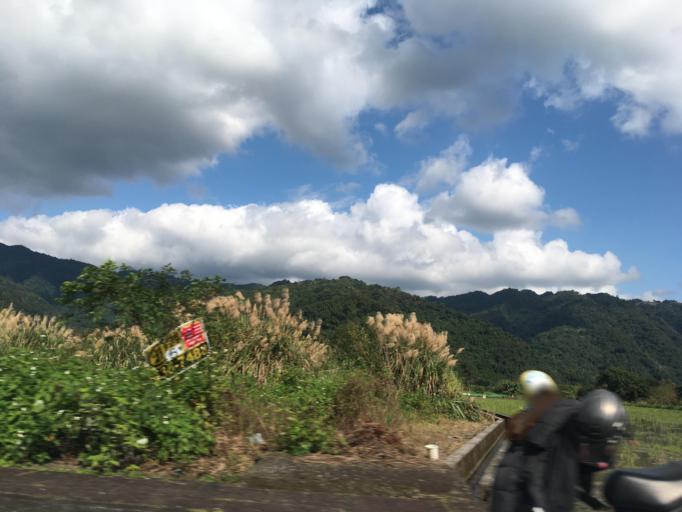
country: TW
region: Taiwan
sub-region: Yilan
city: Yilan
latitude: 24.7492
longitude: 121.6800
